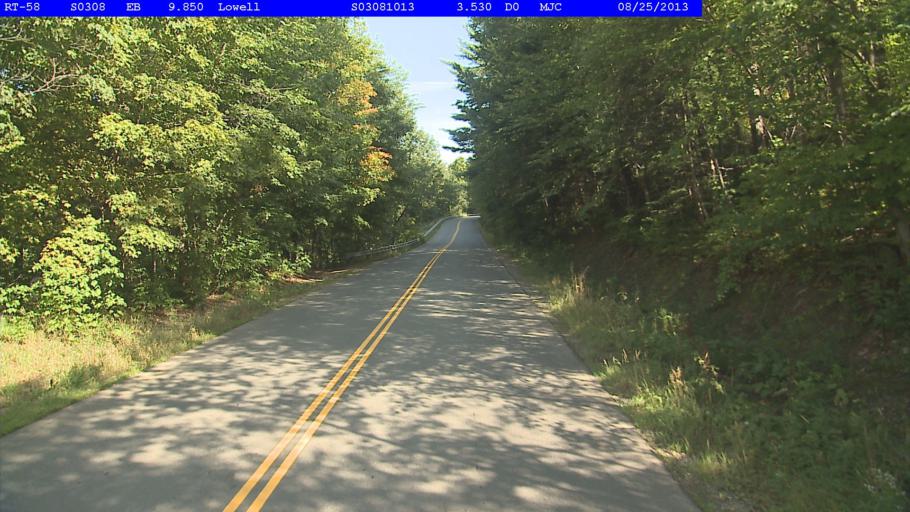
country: US
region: Vermont
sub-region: Lamoille County
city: Hyde Park
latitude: 44.8041
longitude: -72.4576
